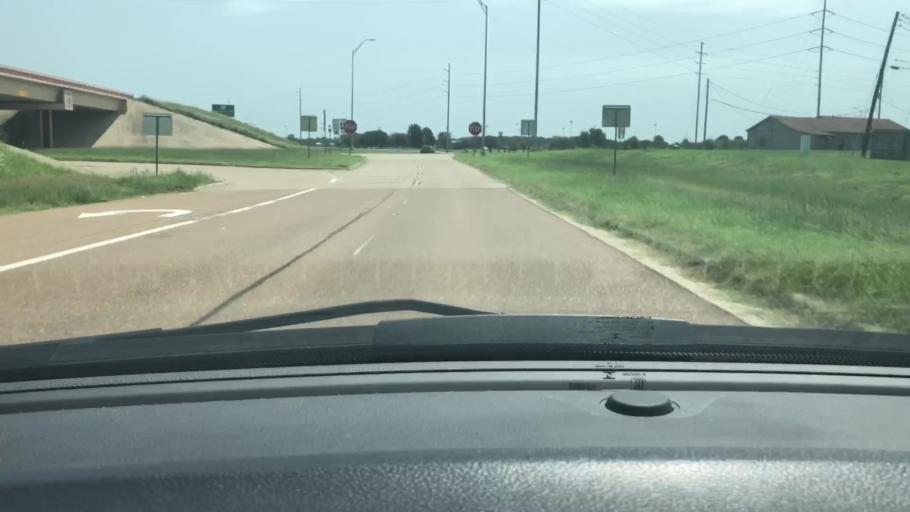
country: US
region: Texas
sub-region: Bowie County
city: Wake Village
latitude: 33.3864
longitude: -94.0930
